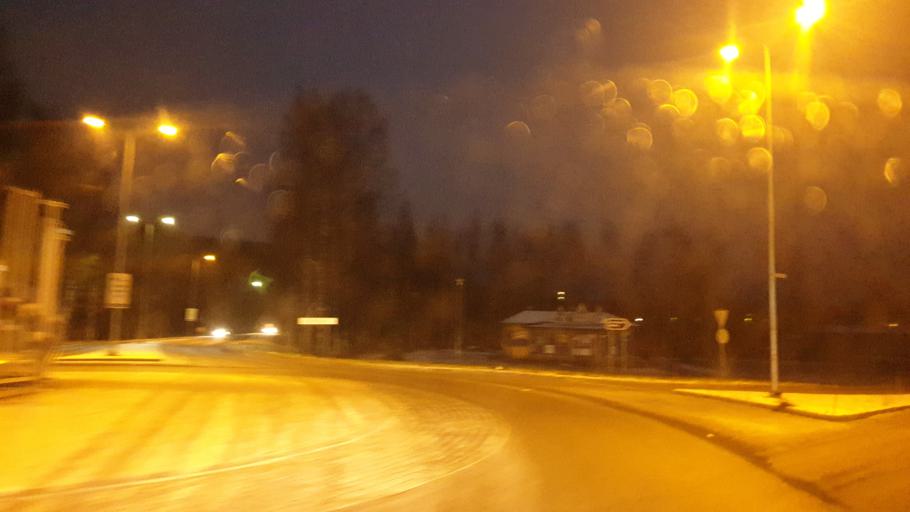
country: FI
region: Southern Savonia
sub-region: Savonlinna
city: Savonlinna
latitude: 61.8655
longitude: 28.9417
